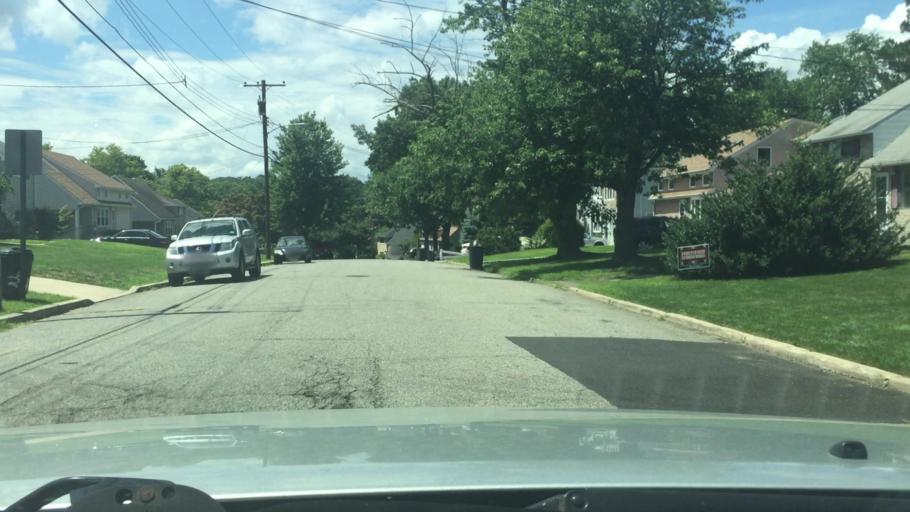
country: US
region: New Jersey
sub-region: Middlesex County
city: Old Bridge
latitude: 40.4148
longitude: -74.3727
